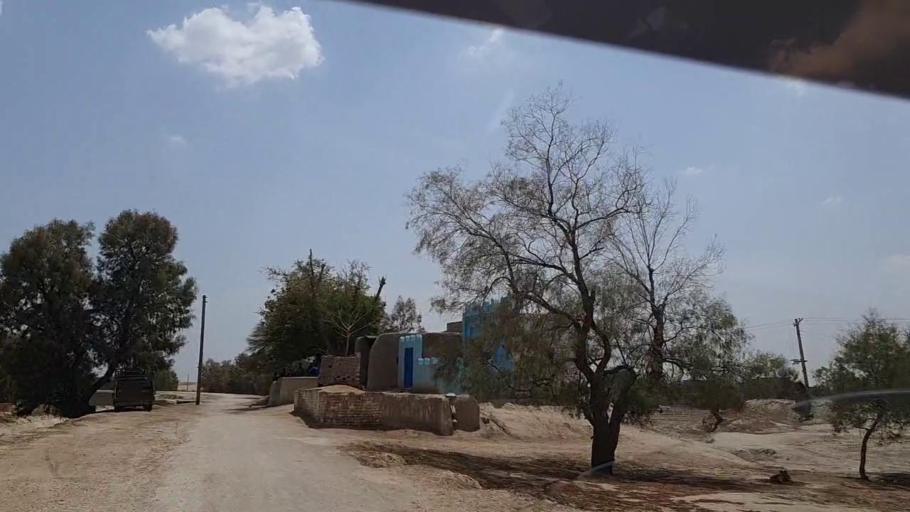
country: PK
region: Sindh
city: Bhan
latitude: 26.5064
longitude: 67.6398
